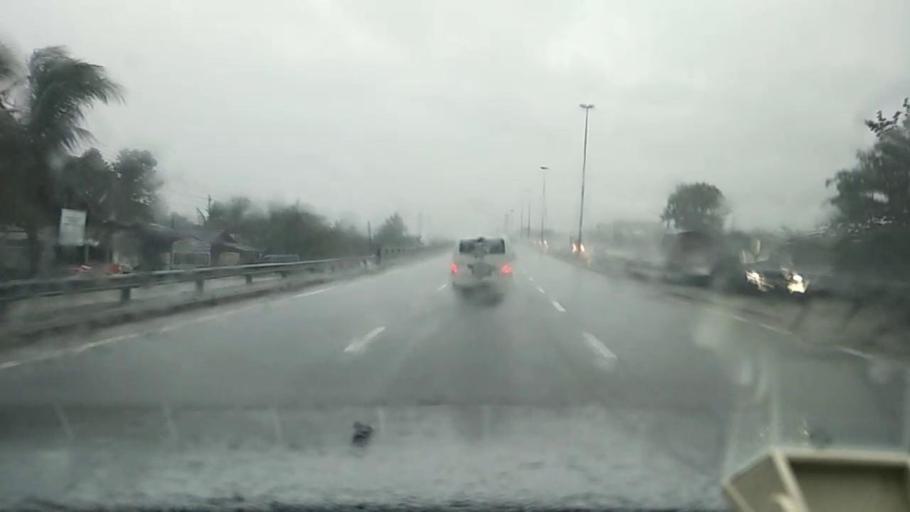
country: MY
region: Selangor
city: Kampong Baharu Balakong
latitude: 2.9842
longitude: 101.7646
